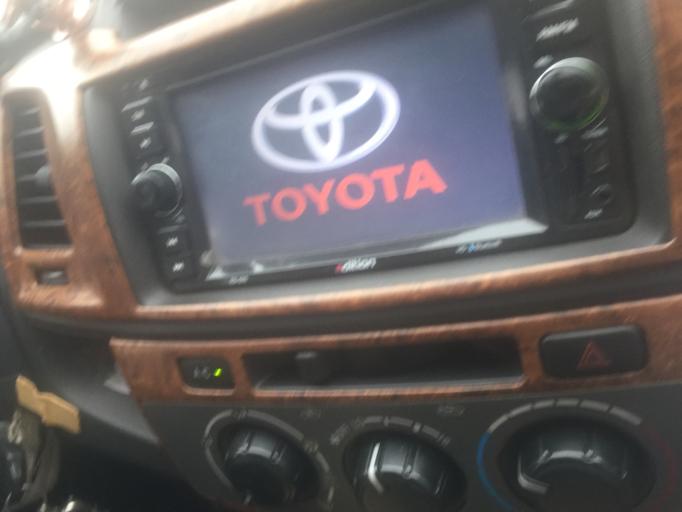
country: LA
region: Xiagnabouli
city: Sainyabuli
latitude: 19.0491
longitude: 101.5281
